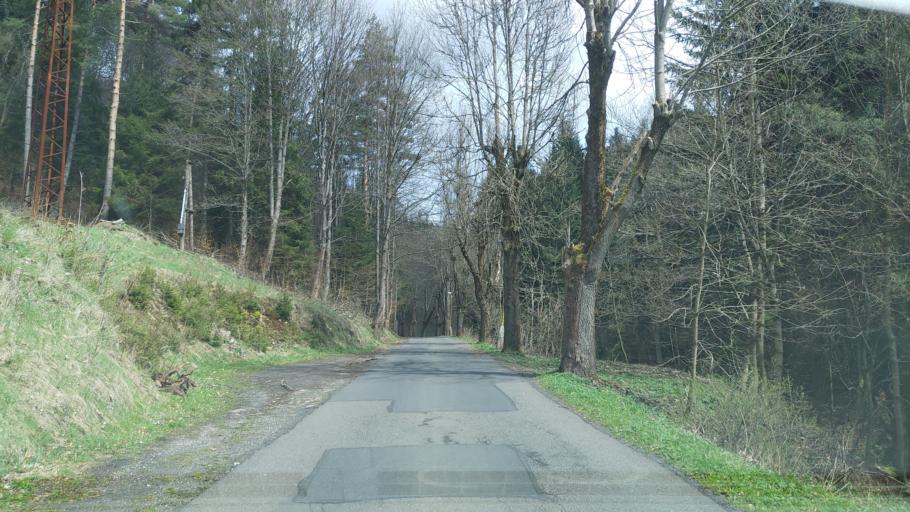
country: CZ
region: Karlovarsky
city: Jachymov
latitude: 50.3617
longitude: 12.9439
